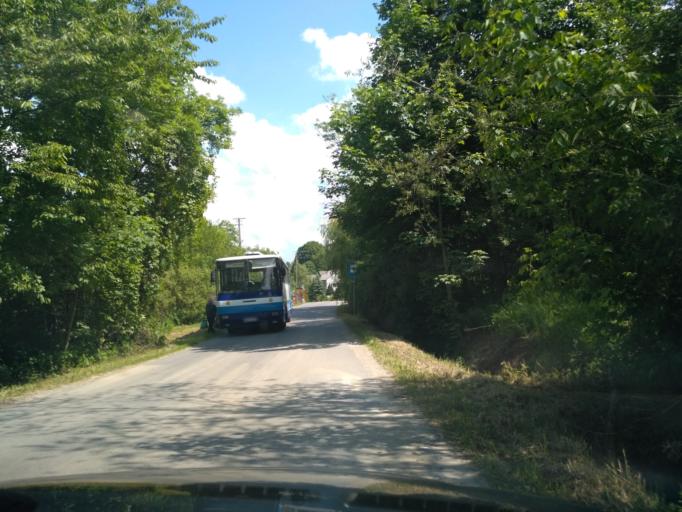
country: PL
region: Subcarpathian Voivodeship
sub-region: Powiat brzozowski
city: Wesola
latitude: 49.8423
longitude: 22.0682
